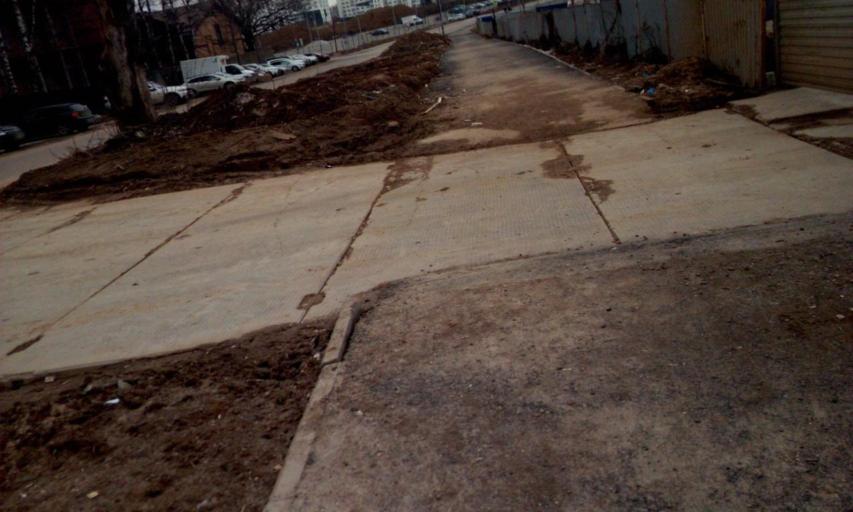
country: RU
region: Moskovskaya
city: Kommunarka
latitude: 55.5549
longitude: 37.5165
